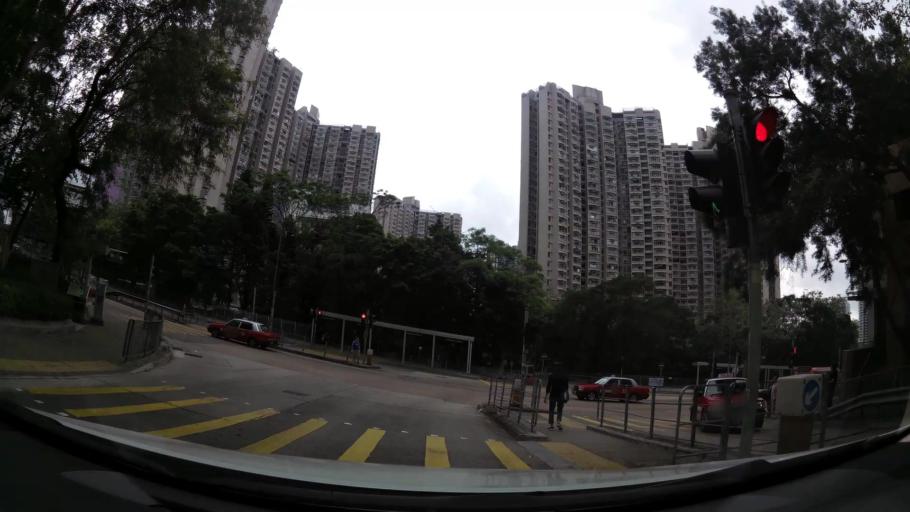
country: HK
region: Wong Tai Sin
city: Wong Tai Sin
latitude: 22.3459
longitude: 114.1994
